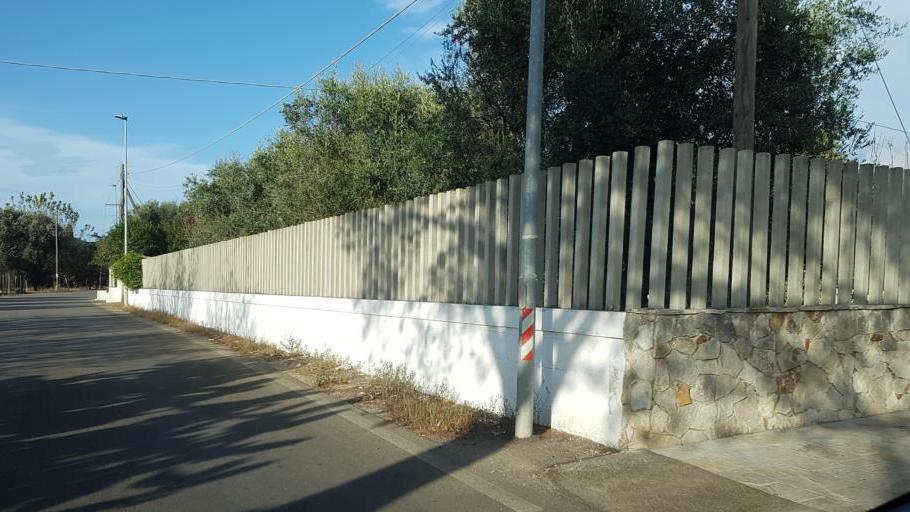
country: IT
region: Apulia
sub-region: Provincia di Brindisi
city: Oria
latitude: 40.5095
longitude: 17.6497
